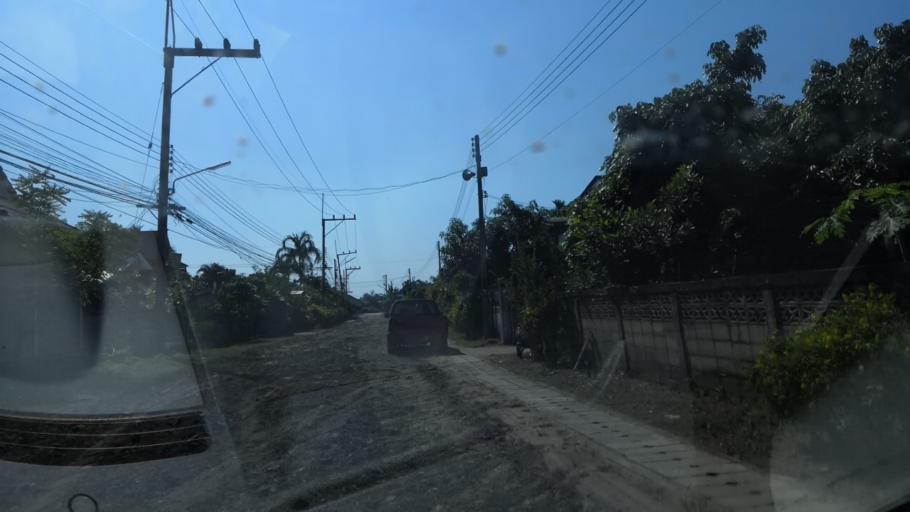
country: TH
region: Chiang Rai
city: Wiang Chai
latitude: 19.8911
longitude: 99.9511
